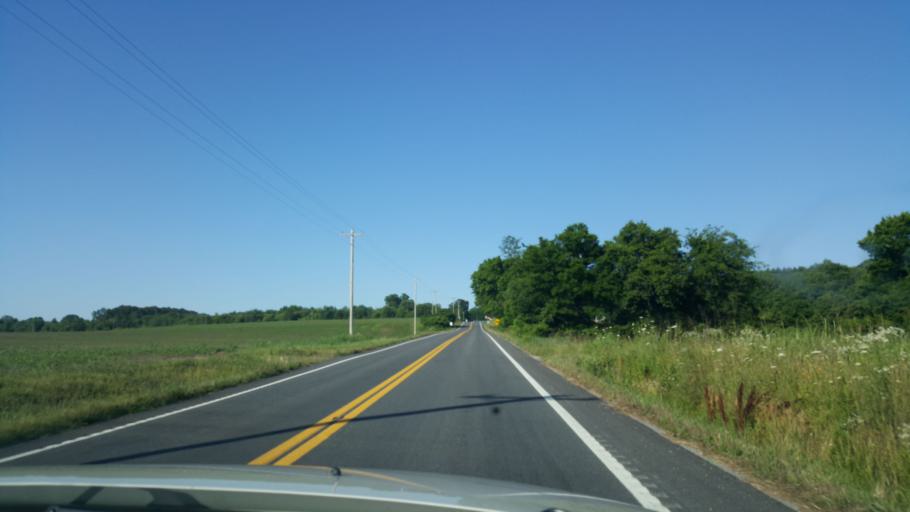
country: US
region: Tennessee
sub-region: Lawrence County
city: Lawrenceburg
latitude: 35.3970
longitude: -87.3880
